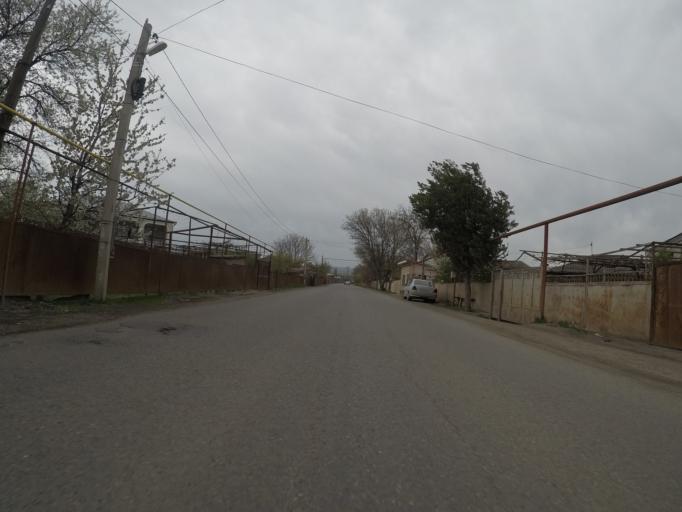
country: GE
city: Agara
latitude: 42.0231
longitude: 43.7219
